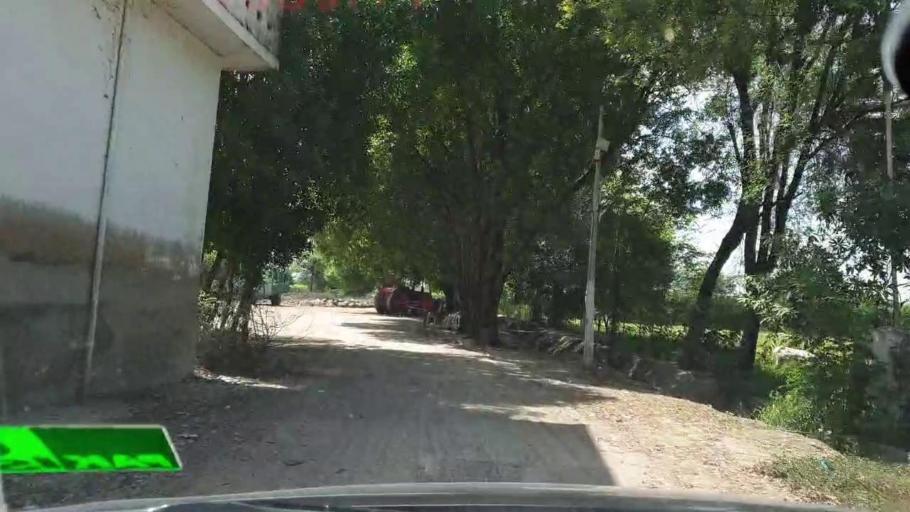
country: PK
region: Sindh
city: Kadhan
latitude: 24.6175
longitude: 69.1825
